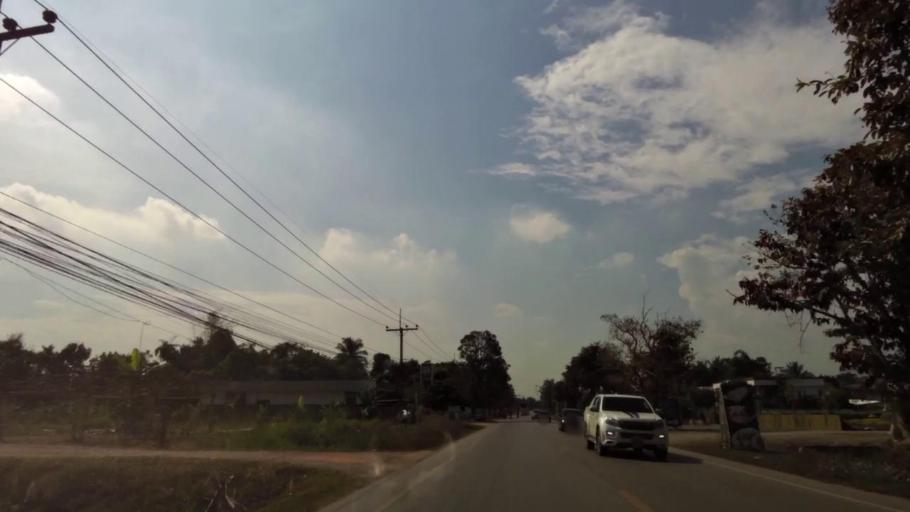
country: TH
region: Chiang Rai
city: Chiang Rai
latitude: 19.8604
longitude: 99.7654
